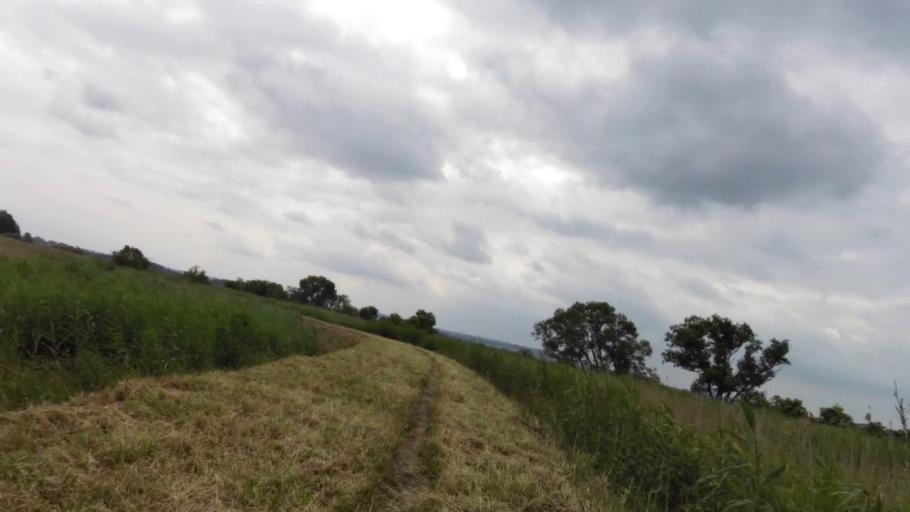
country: PL
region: West Pomeranian Voivodeship
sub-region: Szczecin
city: Szczecin
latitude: 53.4196
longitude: 14.6534
